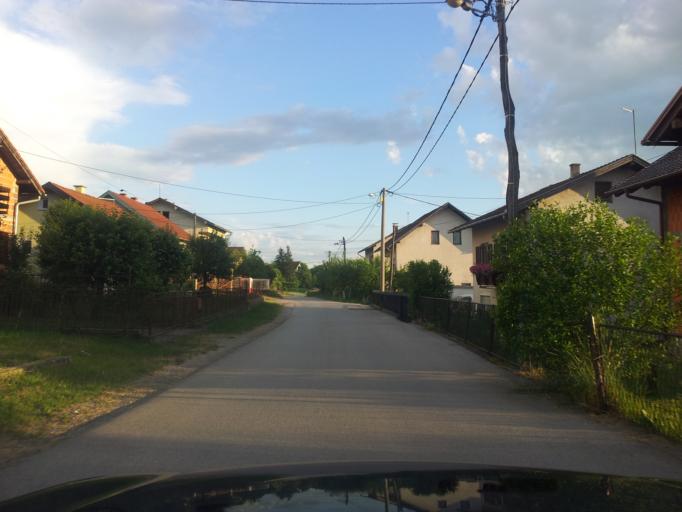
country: HR
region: Karlovacka
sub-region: Grad Karlovac
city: Karlovac
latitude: 45.4617
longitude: 15.5680
